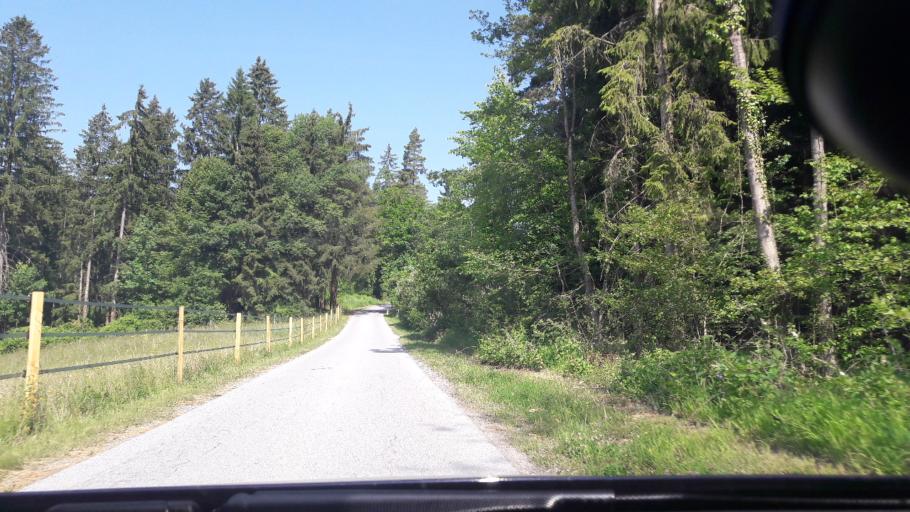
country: AT
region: Styria
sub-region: Politischer Bezirk Graz-Umgebung
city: Stiwoll
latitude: 47.1062
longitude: 15.2013
